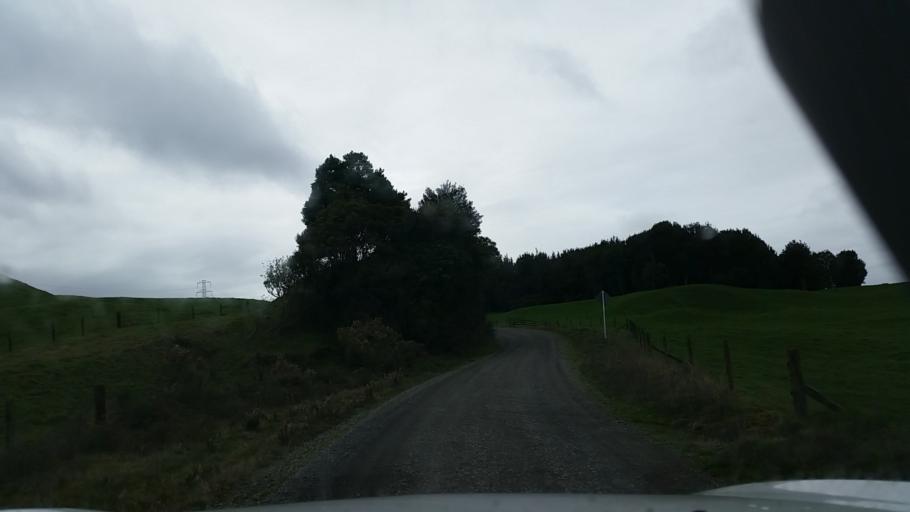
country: NZ
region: Bay of Plenty
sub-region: Rotorua District
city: Rotorua
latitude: -37.9895
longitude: 176.1773
